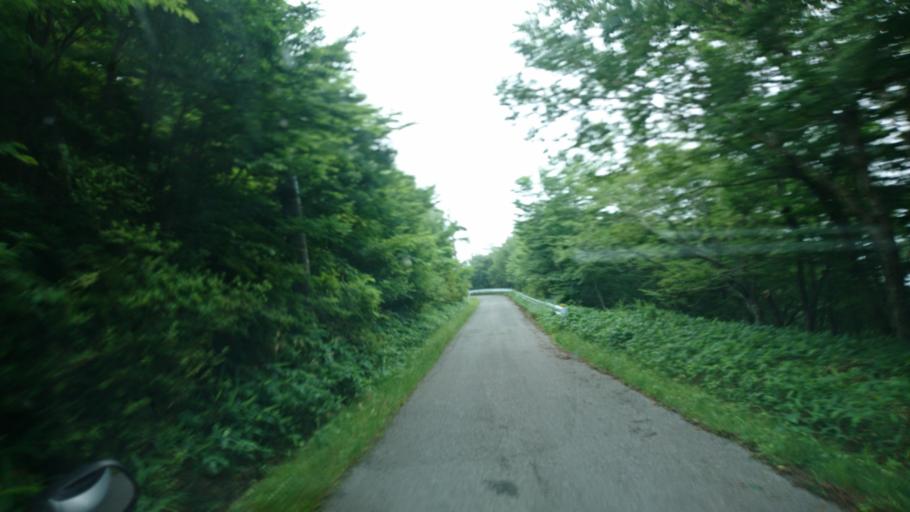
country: JP
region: Iwate
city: Ofunato
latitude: 39.1482
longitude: 141.7540
